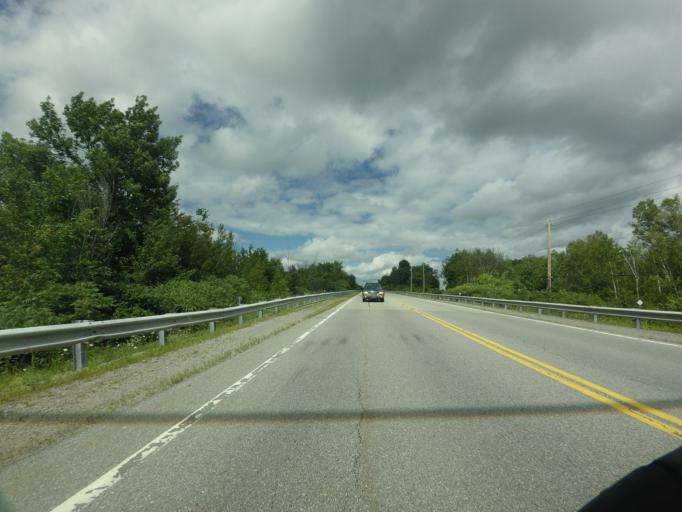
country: CA
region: Ontario
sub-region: Lanark County
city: Smiths Falls
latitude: 44.7783
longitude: -76.1112
